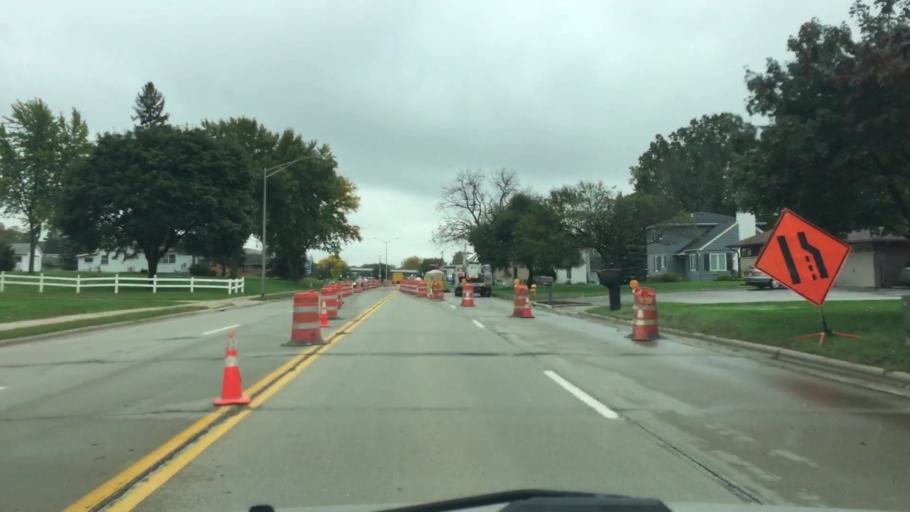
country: US
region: Wisconsin
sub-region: Rock County
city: Janesville
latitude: 42.6986
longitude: -89.0307
